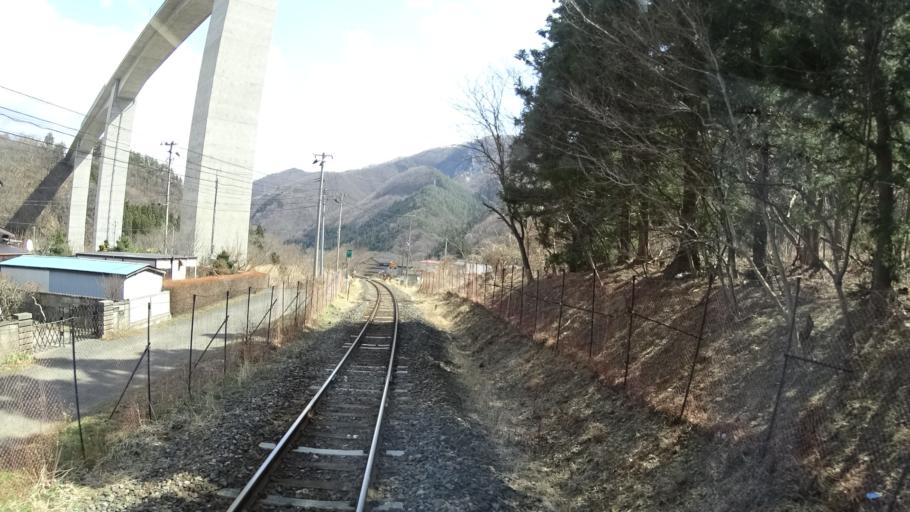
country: JP
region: Iwate
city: Kamaishi
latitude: 39.2519
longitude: 141.7537
